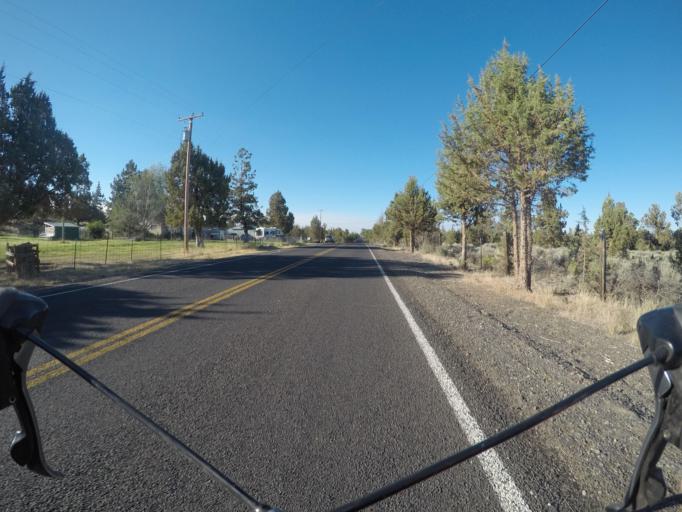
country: US
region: Oregon
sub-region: Deschutes County
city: Redmond
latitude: 44.2527
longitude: -121.2396
